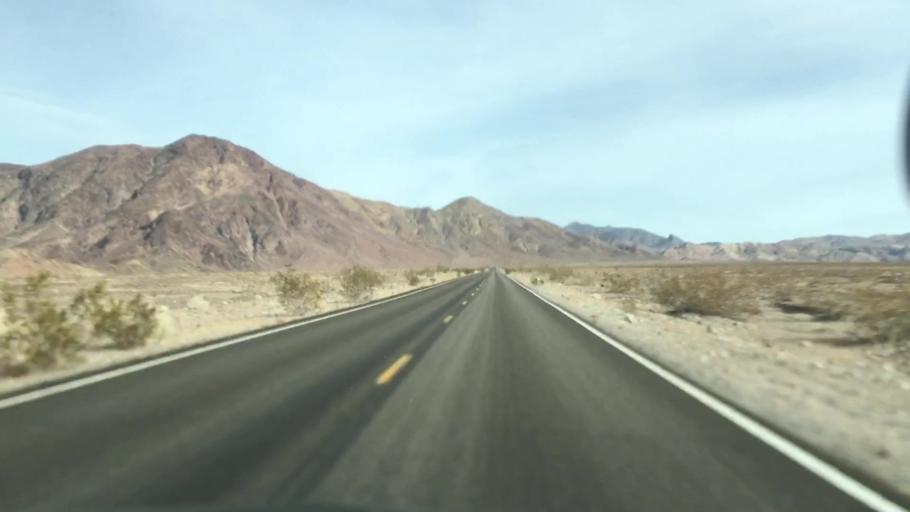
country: US
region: Nevada
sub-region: Nye County
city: Beatty
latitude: 36.6855
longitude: -117.0058
